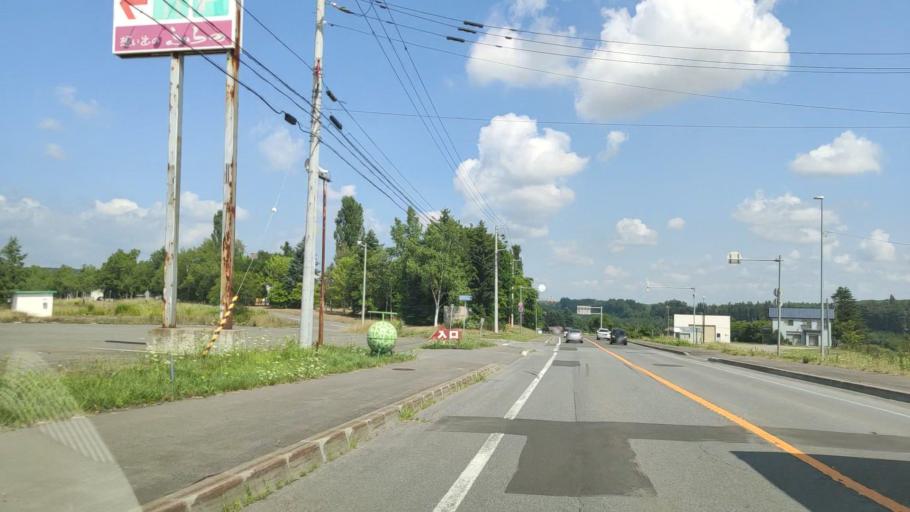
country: JP
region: Hokkaido
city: Shimo-furano
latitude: 43.5204
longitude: 142.4481
